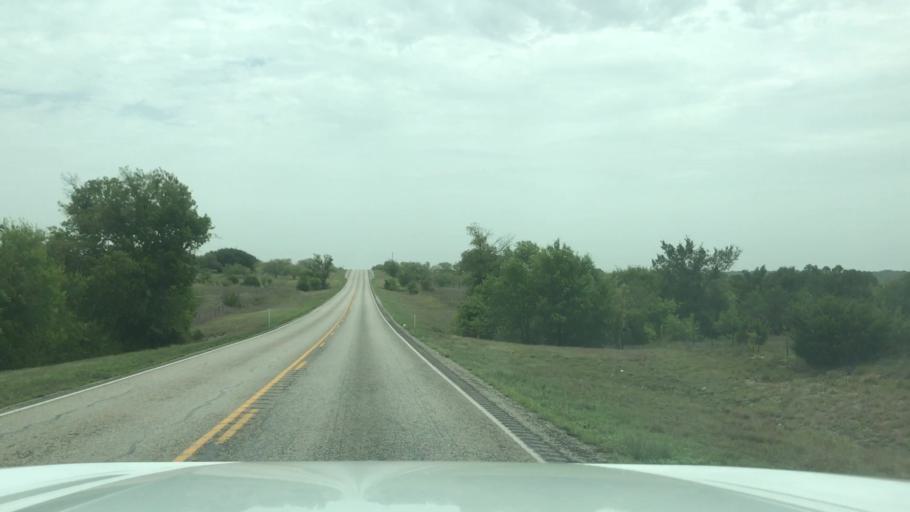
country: US
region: Texas
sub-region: Hamilton County
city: Hico
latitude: 32.0525
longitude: -98.1691
